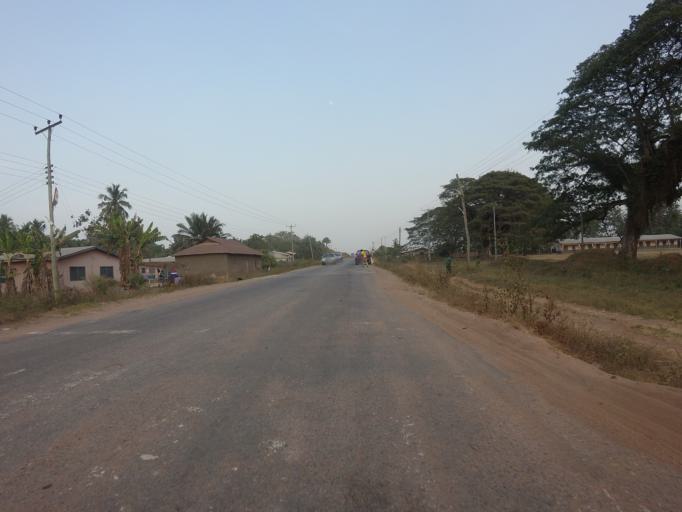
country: GH
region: Volta
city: Ho
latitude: 6.5751
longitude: 0.4166
